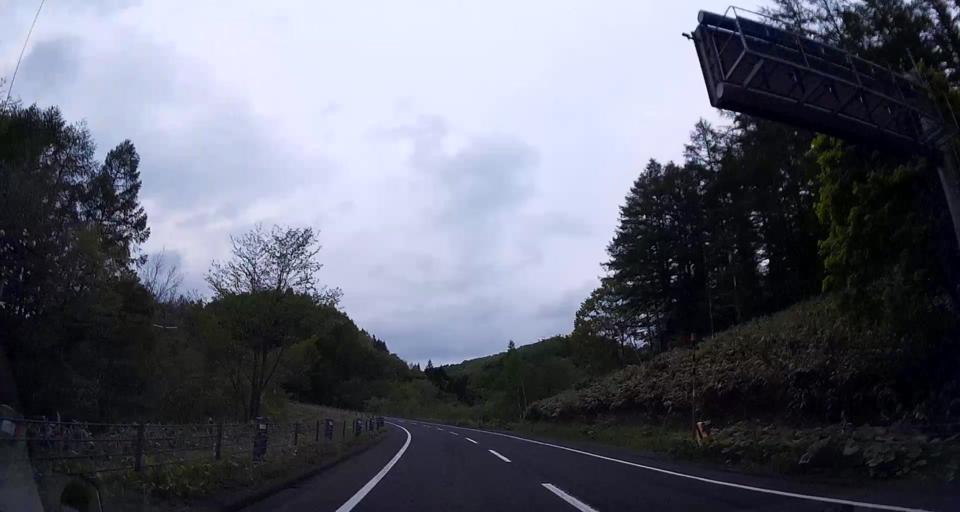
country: JP
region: Hokkaido
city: Shiraoi
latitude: 42.6965
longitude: 141.1029
